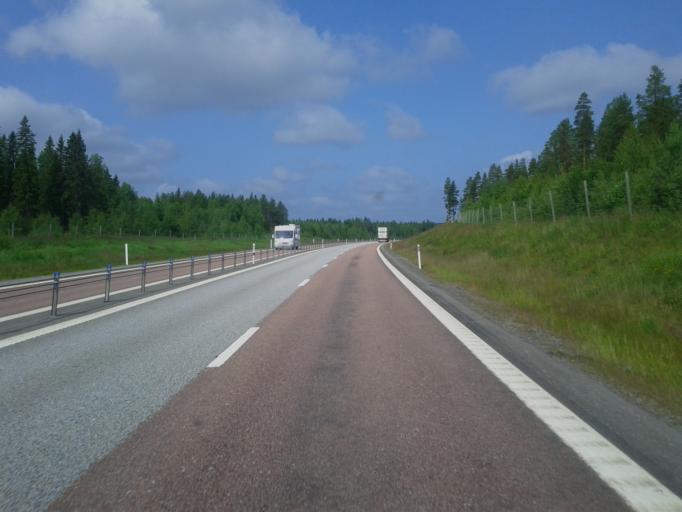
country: SE
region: Vaesterbotten
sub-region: Skelleftea Kommun
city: Skelleftea
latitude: 64.6979
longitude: 21.0109
